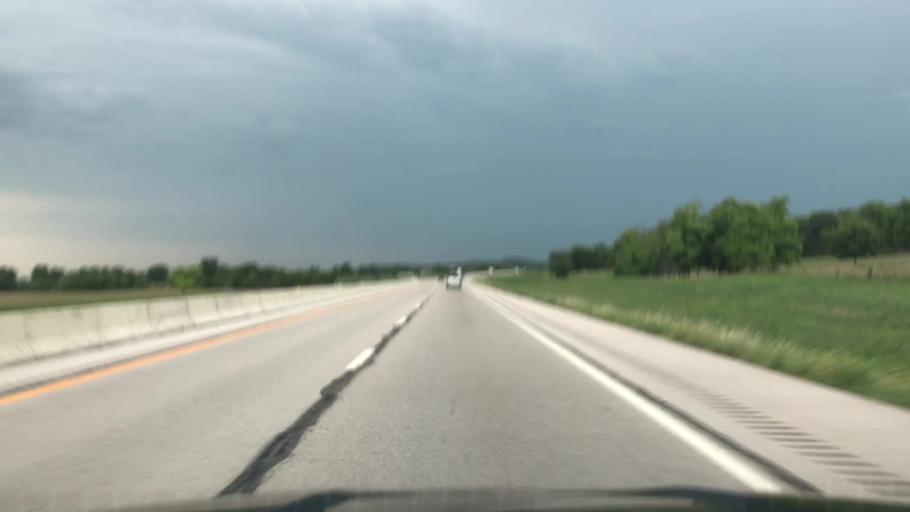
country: US
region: Oklahoma
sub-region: Rogers County
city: Bushyhead
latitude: 36.3581
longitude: -95.4553
